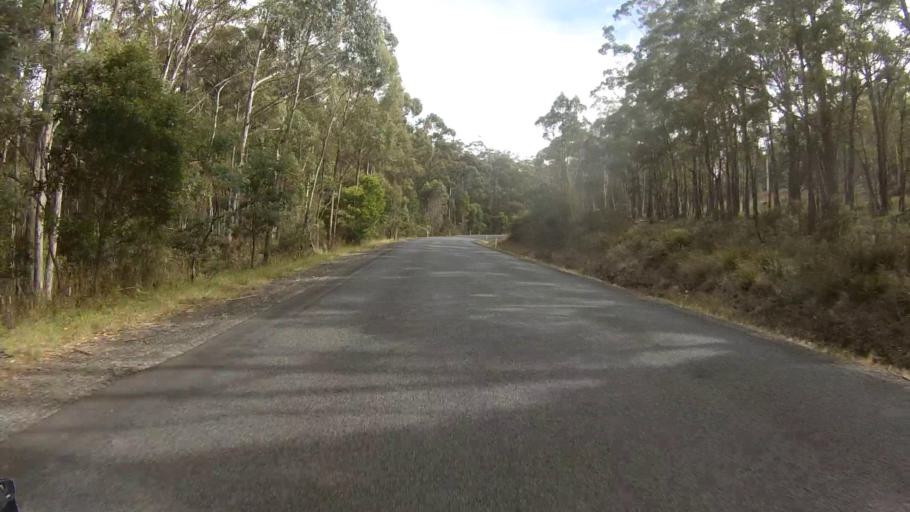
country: AU
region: Tasmania
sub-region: Sorell
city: Sorell
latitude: -42.8139
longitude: 147.7922
